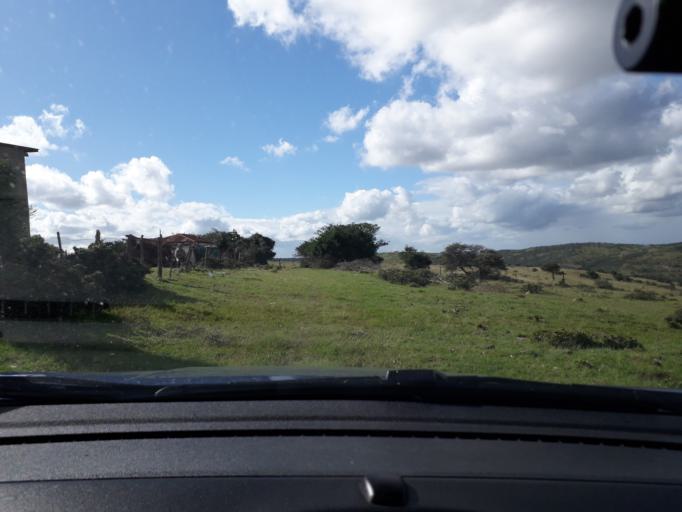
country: ZA
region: Eastern Cape
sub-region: Buffalo City Metropolitan Municipality
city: Bhisho
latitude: -33.1122
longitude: 27.4314
